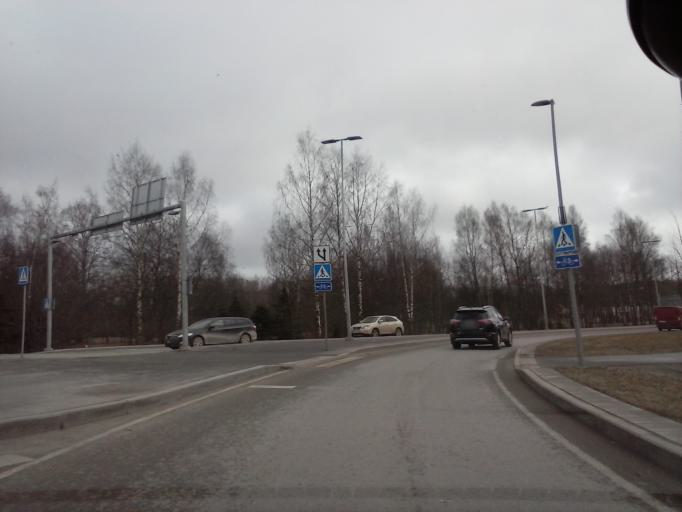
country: EE
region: Harju
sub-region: Saue vald
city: Laagri
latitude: 59.4229
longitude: 24.6466
